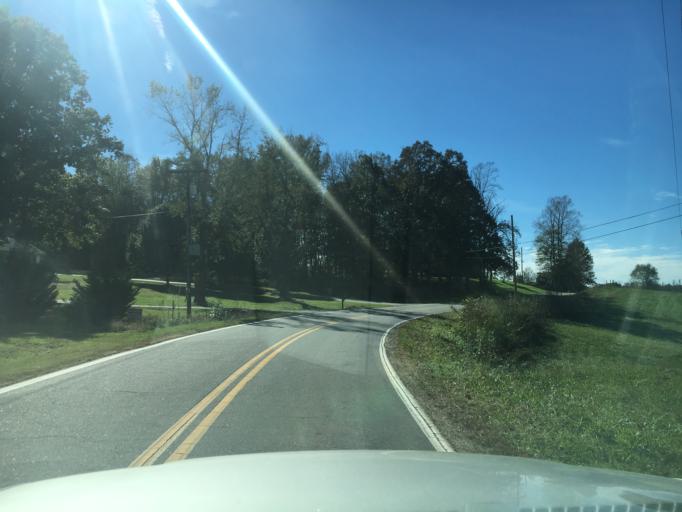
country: US
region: North Carolina
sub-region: Burke County
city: Salem
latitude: 35.7208
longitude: -81.7170
